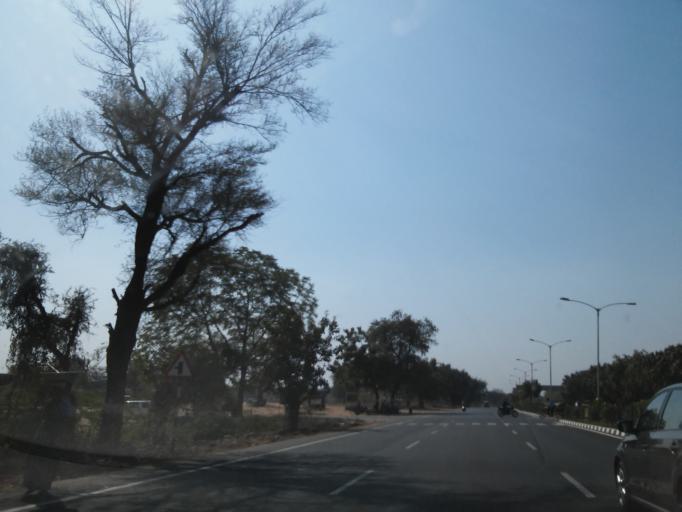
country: IN
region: Gujarat
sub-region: Gandhinagar
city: Ghandinagar
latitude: 23.2028
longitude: 72.6578
